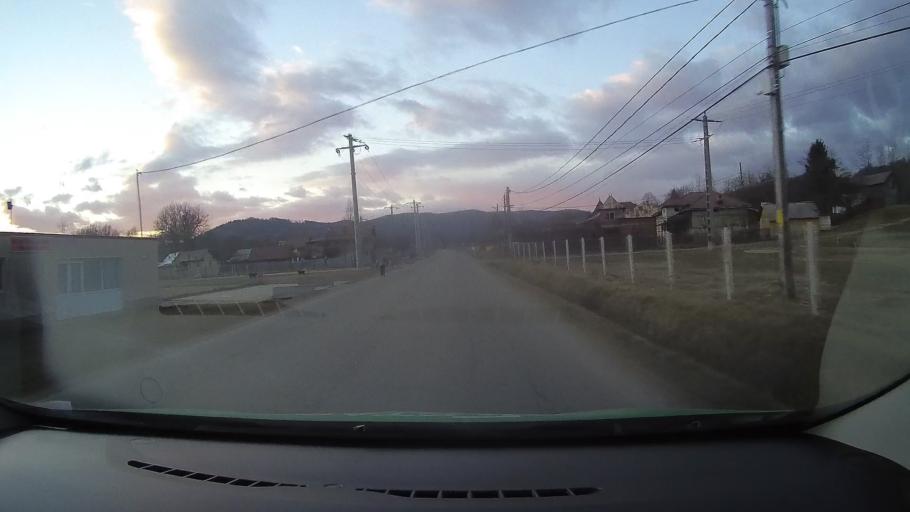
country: RO
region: Dambovita
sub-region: Comuna Valea Lunga
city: Valea Lunga-Cricov
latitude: 45.0635
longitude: 25.5878
